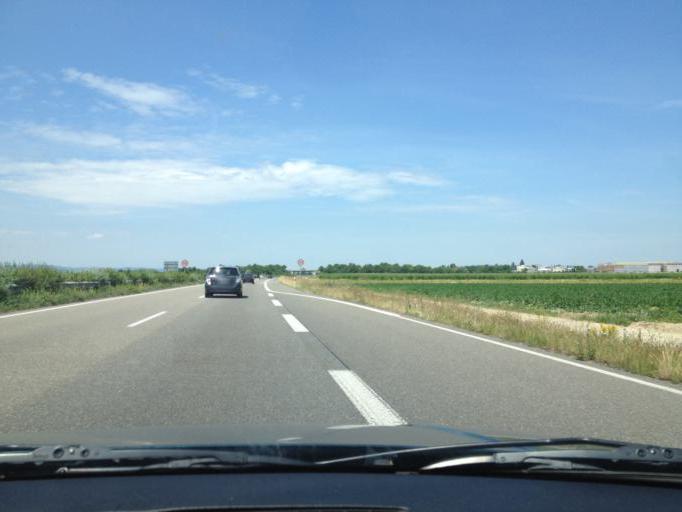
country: DE
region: Rheinland-Pfalz
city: Limburgerhof
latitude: 49.4385
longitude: 8.3828
